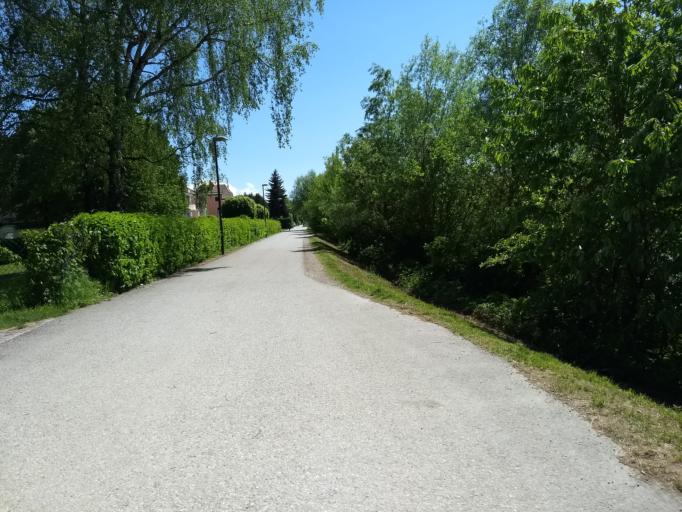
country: AT
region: Salzburg
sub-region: Politischer Bezirk Salzburg-Umgebung
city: Bergheim
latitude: 47.8249
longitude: 13.0330
